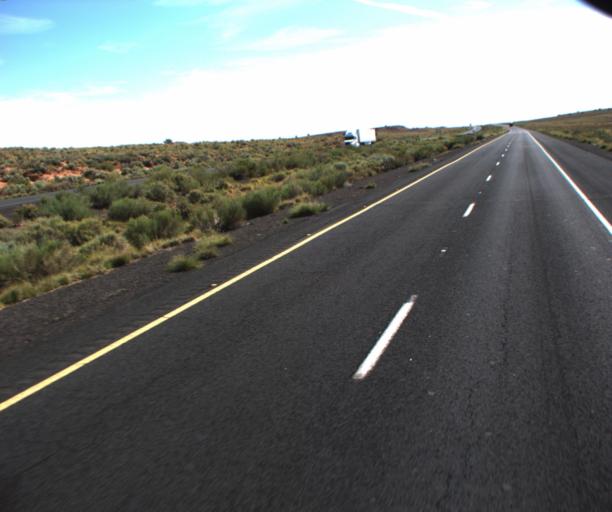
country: US
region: Arizona
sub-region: Apache County
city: Houck
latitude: 35.1018
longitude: -109.6240
